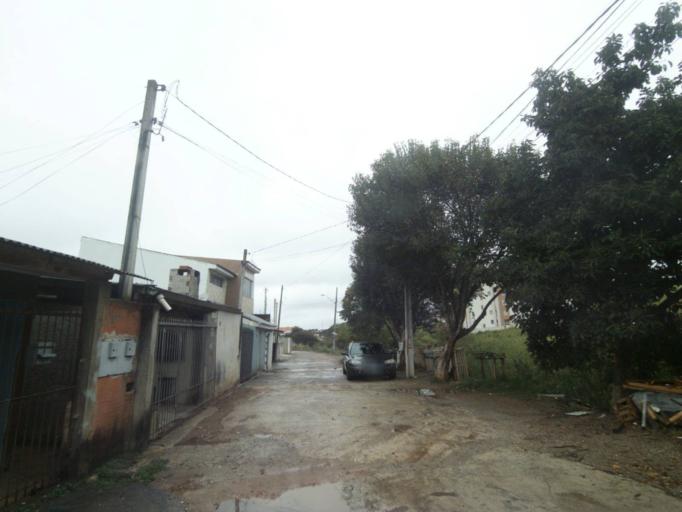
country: BR
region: Parana
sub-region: Curitiba
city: Curitiba
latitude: -25.5028
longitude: -49.3077
